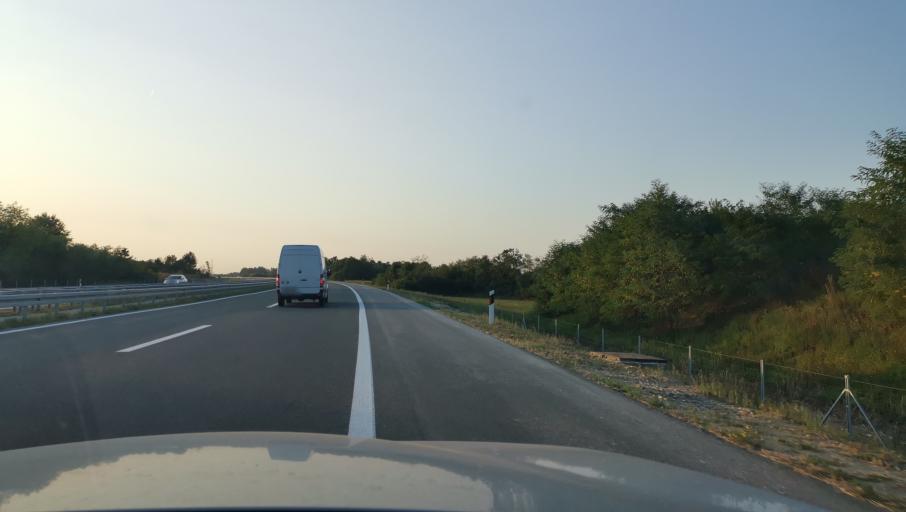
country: RS
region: Central Serbia
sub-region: Kolubarski Okrug
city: Lajkovac
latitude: 44.3792
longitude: 20.1160
